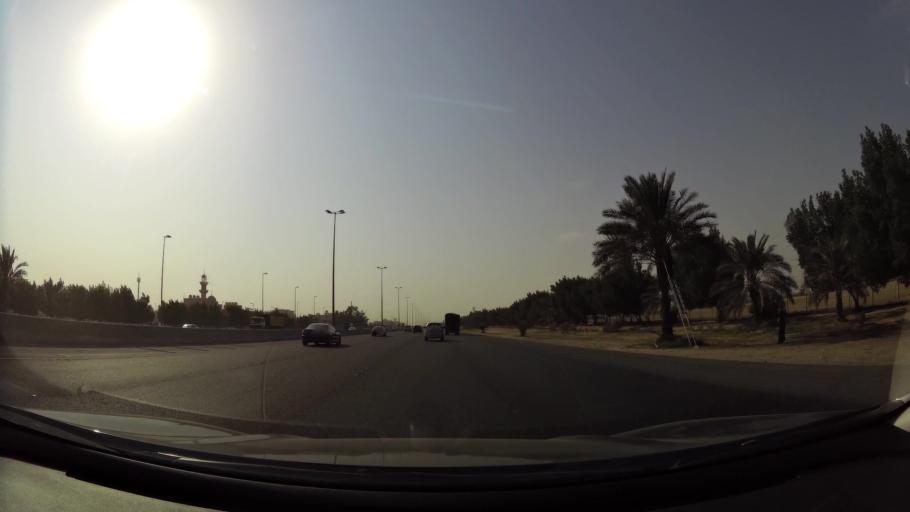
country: KW
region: Al Ahmadi
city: Al Ahmadi
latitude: 29.1072
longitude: 48.0956
